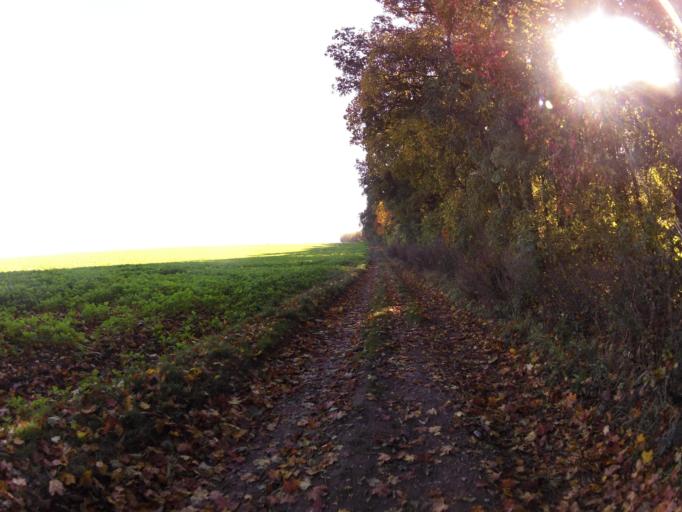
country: DE
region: Bavaria
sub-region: Regierungsbezirk Unterfranken
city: Kirchheim
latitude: 49.6659
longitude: 9.8815
